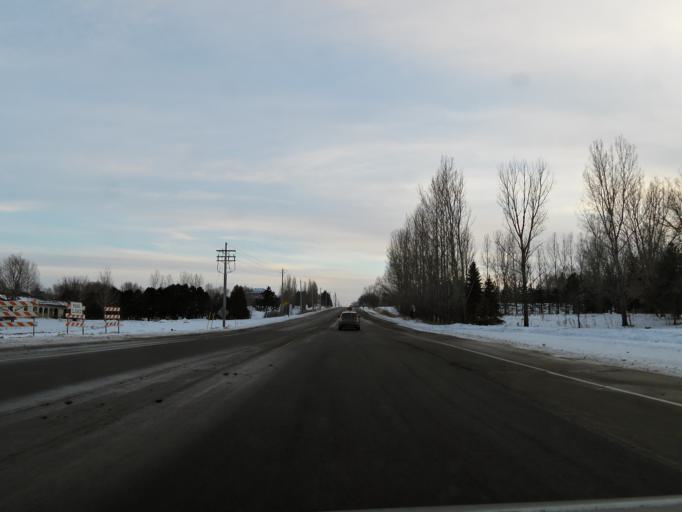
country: US
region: Minnesota
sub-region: Scott County
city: Shakopee
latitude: 44.7580
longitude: -93.5053
